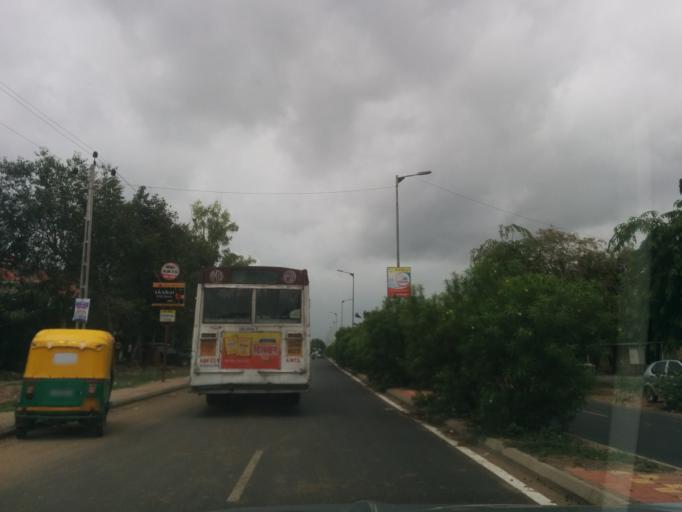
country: IN
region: Gujarat
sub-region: Ahmadabad
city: Sarkhej
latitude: 23.0518
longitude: 72.4864
